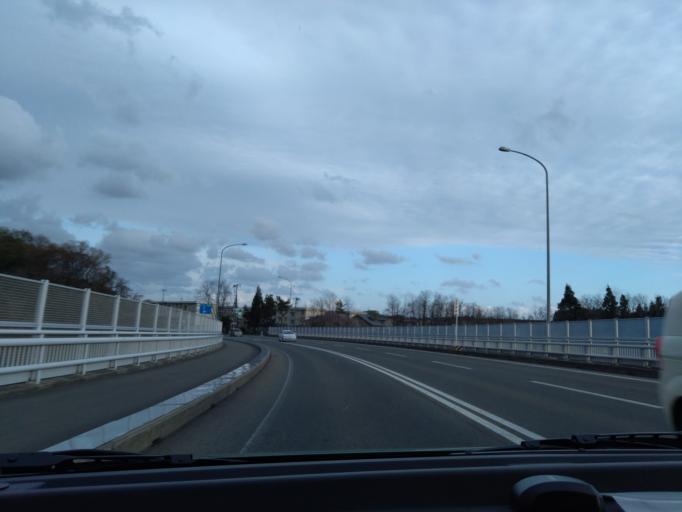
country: JP
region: Akita
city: Akita
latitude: 39.7348
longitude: 140.1371
